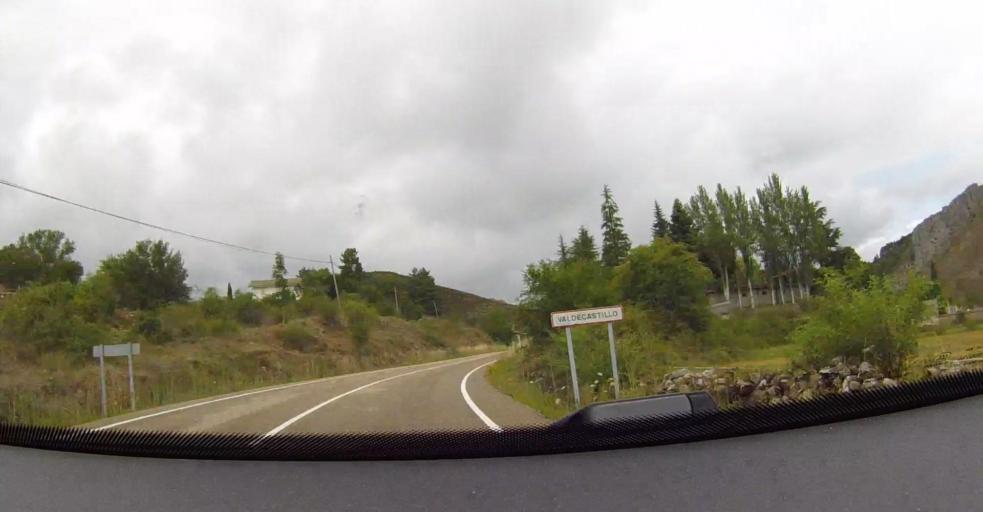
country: ES
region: Castille and Leon
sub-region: Provincia de Leon
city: Bonar
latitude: 42.9046
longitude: -5.3126
